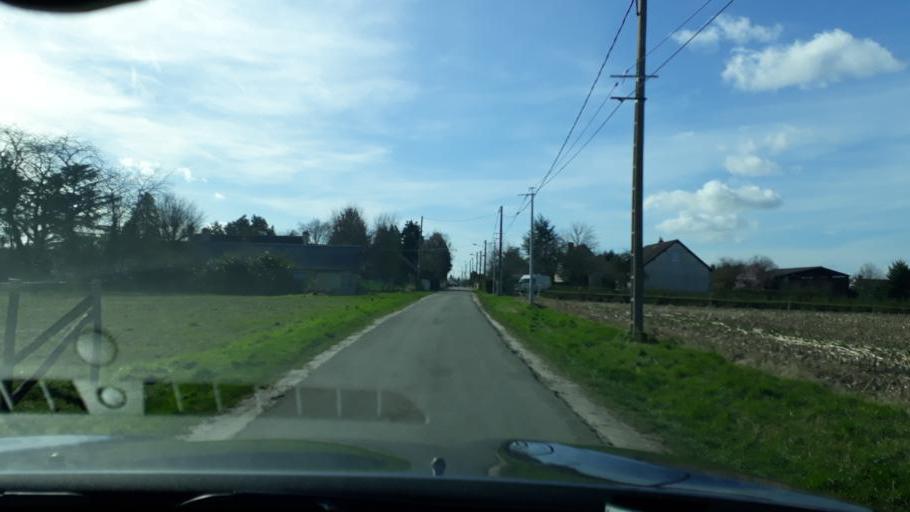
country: FR
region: Centre
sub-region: Departement du Loiret
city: Trainou
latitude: 47.9808
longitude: 2.1104
